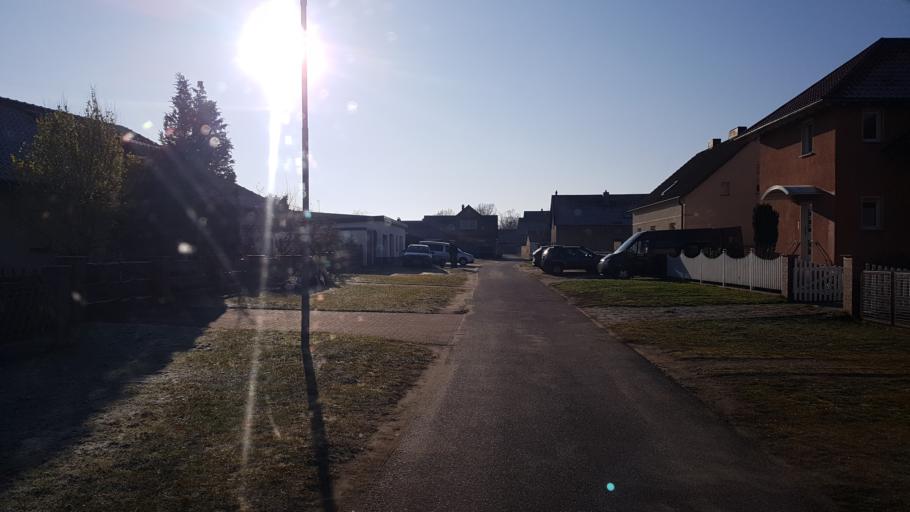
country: DE
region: Brandenburg
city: Sallgast
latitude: 51.5897
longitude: 13.8503
